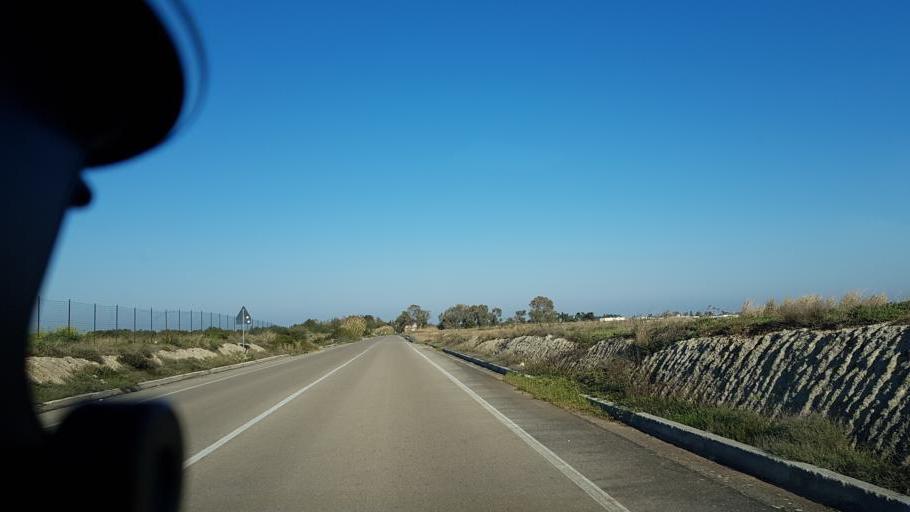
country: IT
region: Apulia
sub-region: Provincia di Lecce
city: Merine
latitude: 40.3942
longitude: 18.2657
